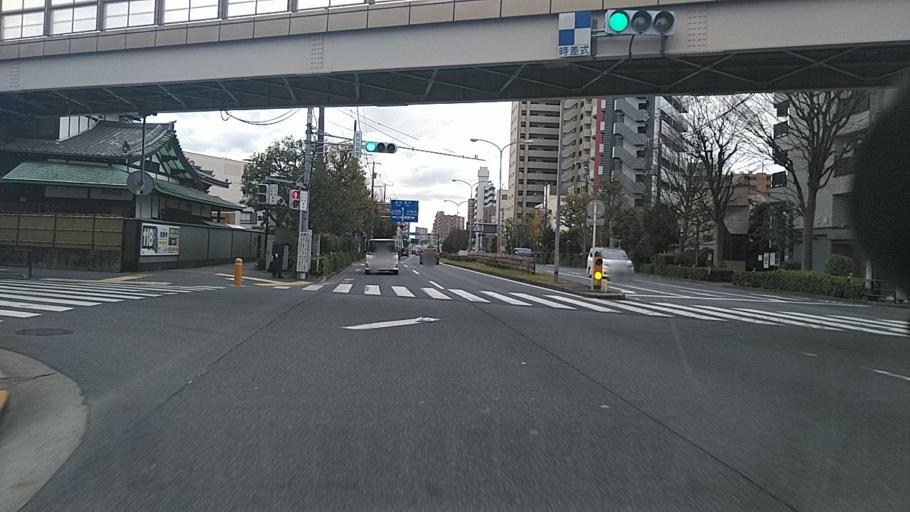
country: JP
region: Chiba
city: Matsudo
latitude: 35.7653
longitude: 139.8508
